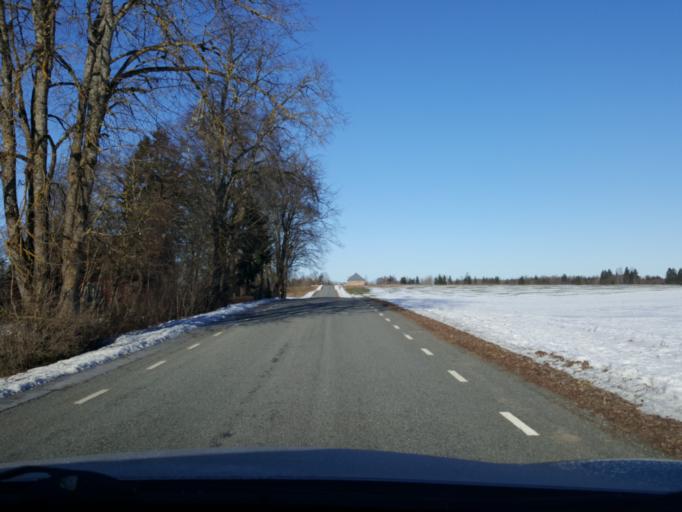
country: EE
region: Viljandimaa
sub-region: Viljandi linn
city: Viljandi
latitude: 58.4127
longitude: 25.5542
